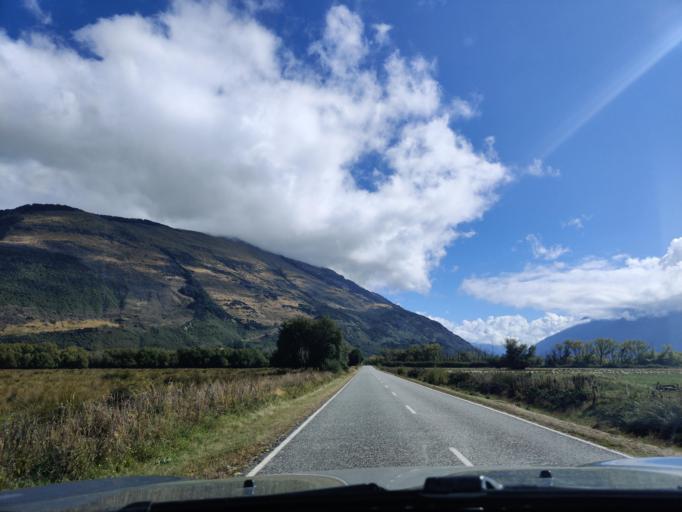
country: NZ
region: Otago
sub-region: Queenstown-Lakes District
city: Queenstown
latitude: -44.7914
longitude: 168.4004
